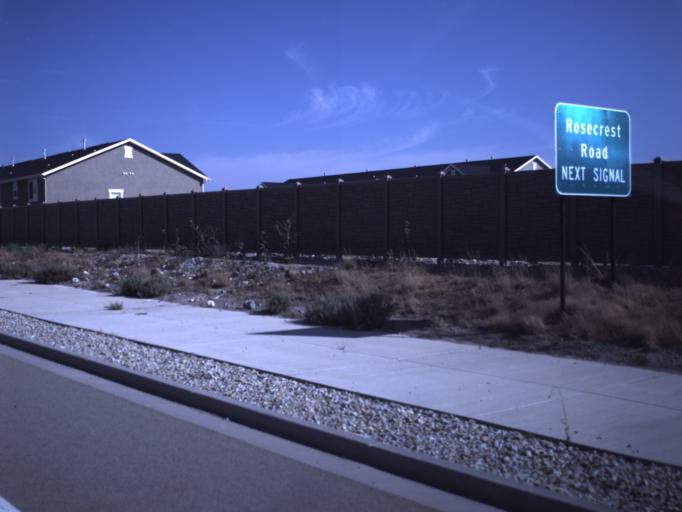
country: US
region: Utah
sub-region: Salt Lake County
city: Herriman
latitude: 40.4868
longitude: -111.9955
